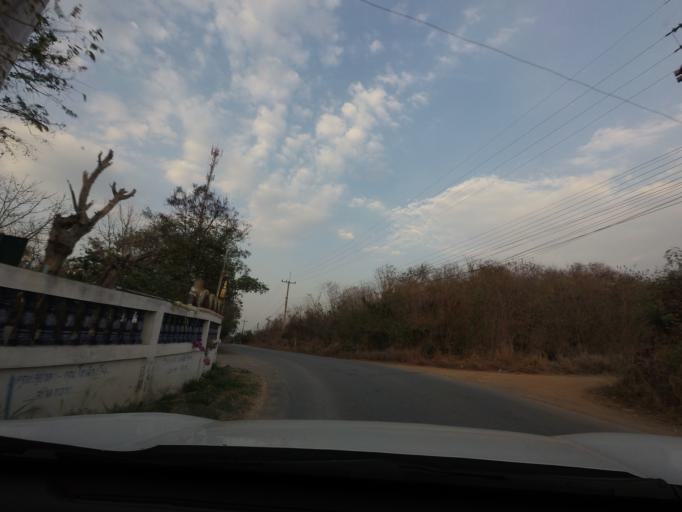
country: TH
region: Nakhon Ratchasima
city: Pak Chong
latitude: 14.6478
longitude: 101.4661
